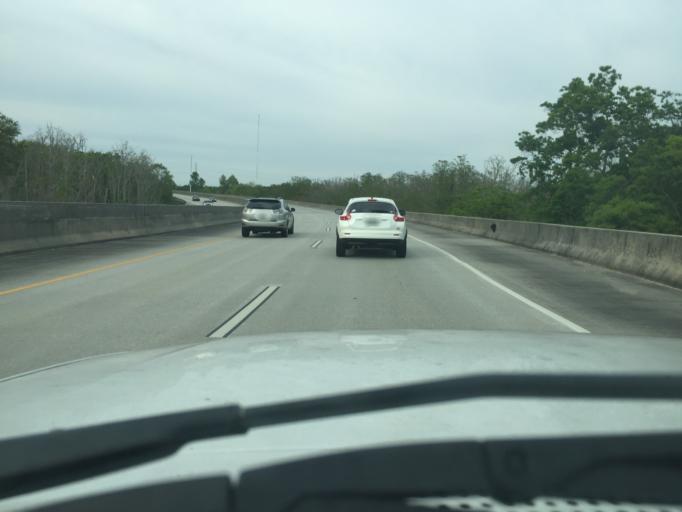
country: US
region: Georgia
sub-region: Chatham County
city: Savannah
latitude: 32.0695
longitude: -81.0747
